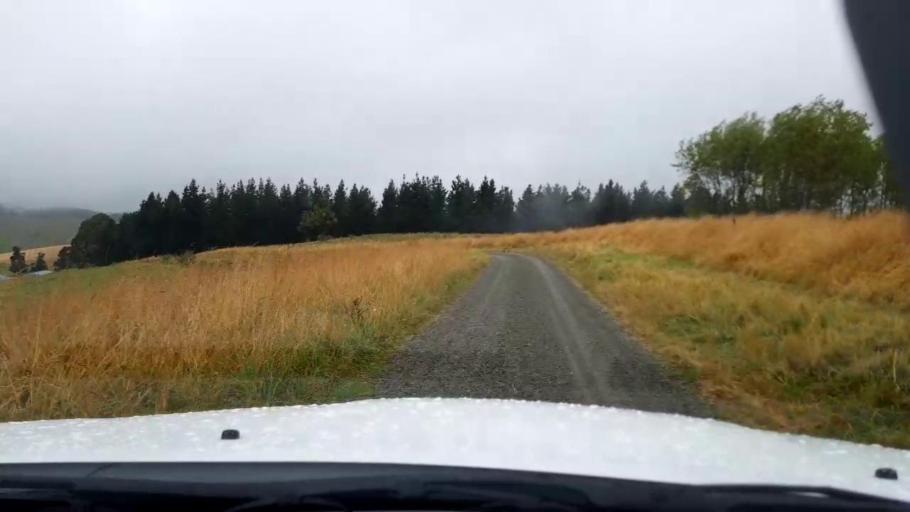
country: NZ
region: Canterbury
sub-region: Timaru District
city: Pleasant Point
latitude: -44.1773
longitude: 171.0922
